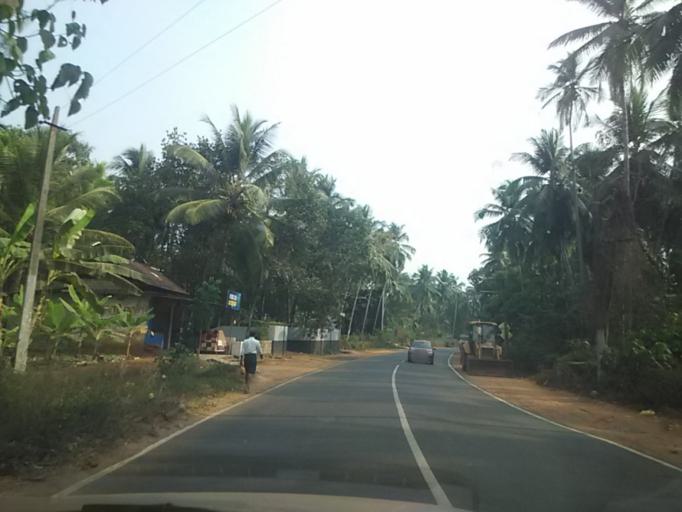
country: IN
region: Kerala
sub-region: Kozhikode
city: Naduvannur
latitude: 11.4789
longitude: 75.7749
